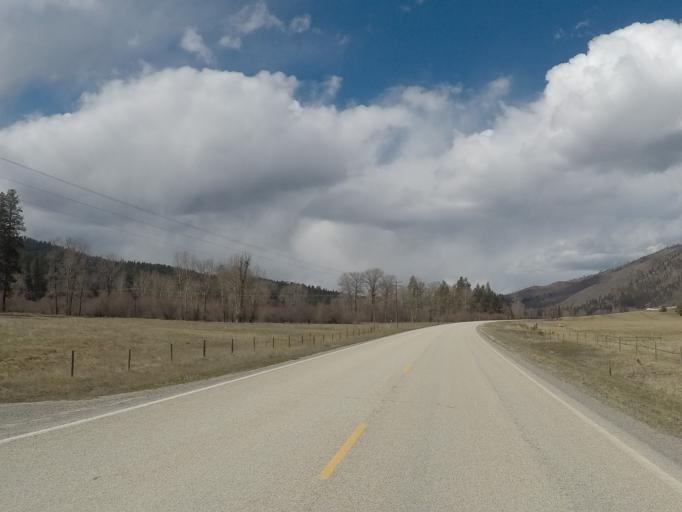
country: US
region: Montana
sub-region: Missoula County
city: Lolo
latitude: 46.7560
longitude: -114.2456
